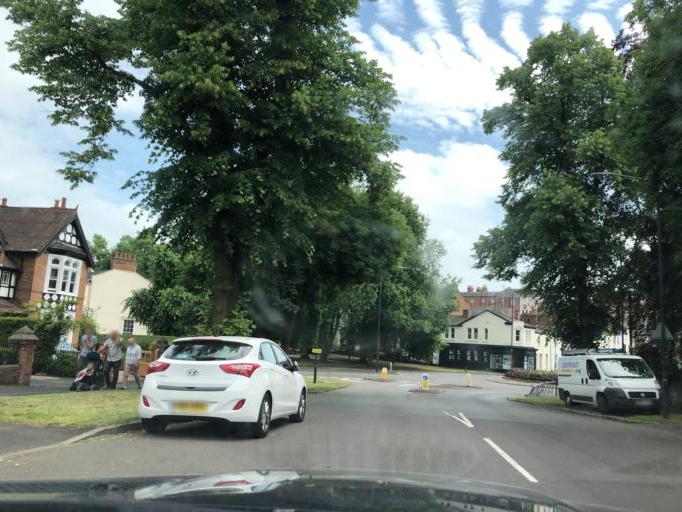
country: GB
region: England
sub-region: Warwickshire
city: Royal Leamington Spa
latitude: 52.2966
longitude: -1.5406
